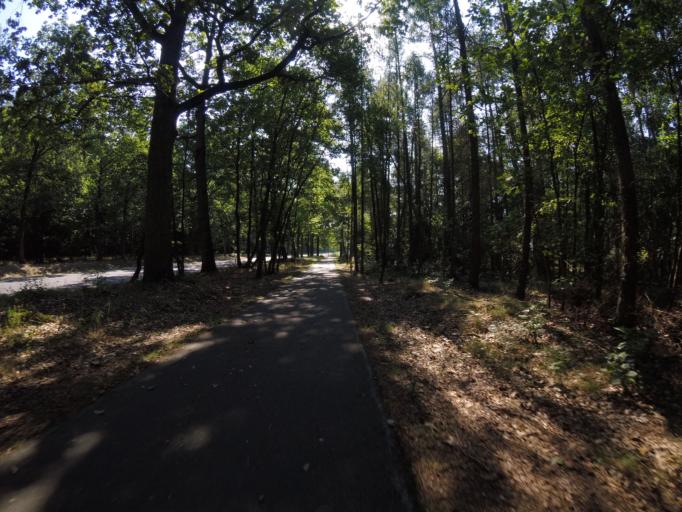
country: DE
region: Brandenburg
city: Mullrose
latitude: 52.2575
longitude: 14.3892
